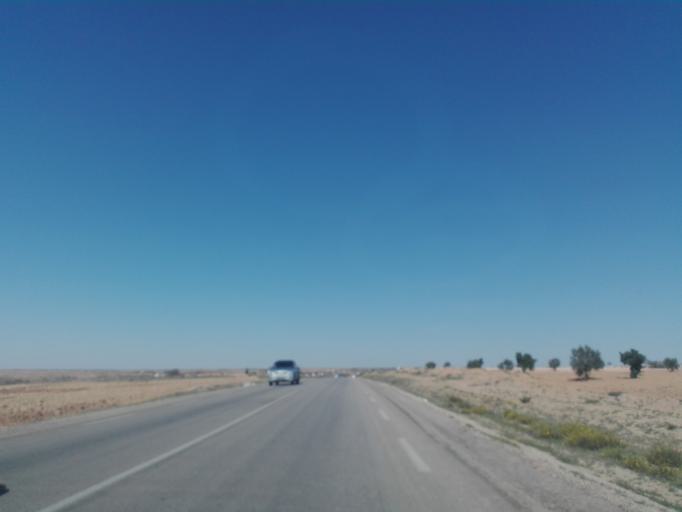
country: TN
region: Safaqis
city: Bi'r `Ali Bin Khalifah
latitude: 34.7402
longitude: 10.3931
